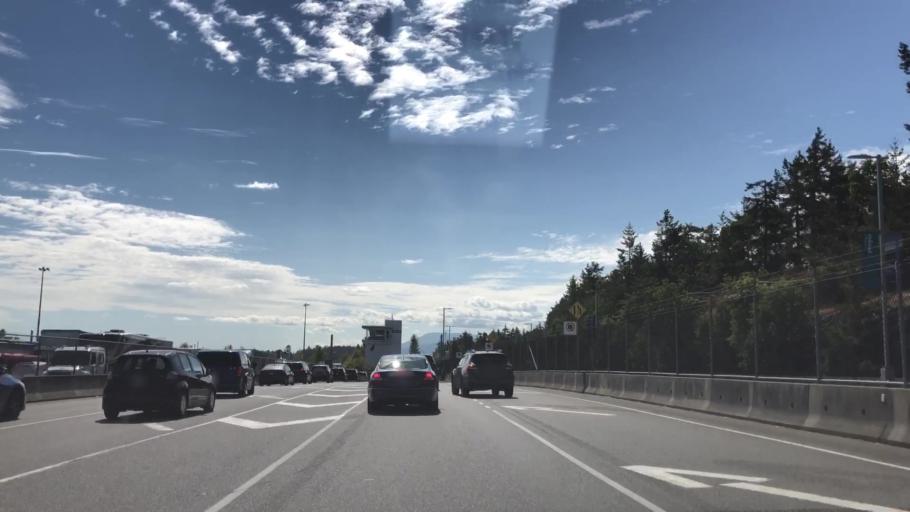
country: CA
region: British Columbia
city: Nanaimo
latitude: 49.1606
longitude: -123.8924
